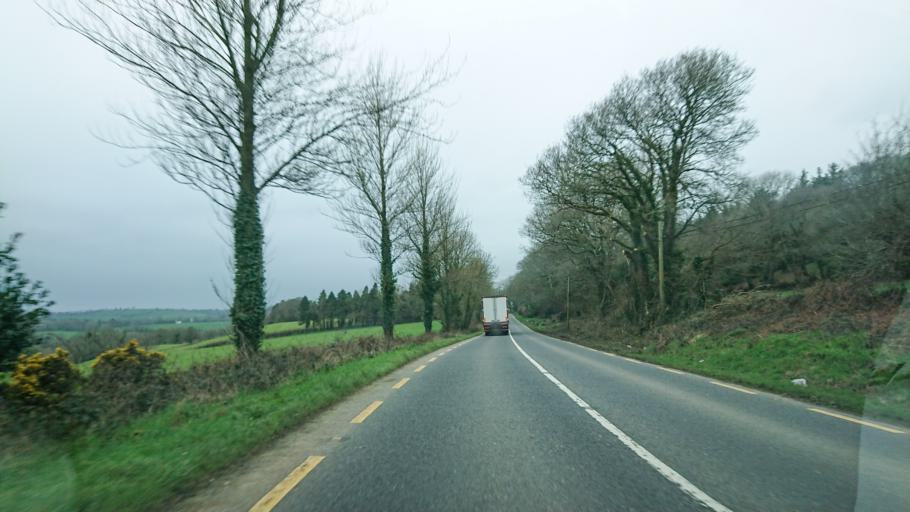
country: IE
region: Munster
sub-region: County Cork
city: Bandon
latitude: 51.7440
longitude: -8.8042
